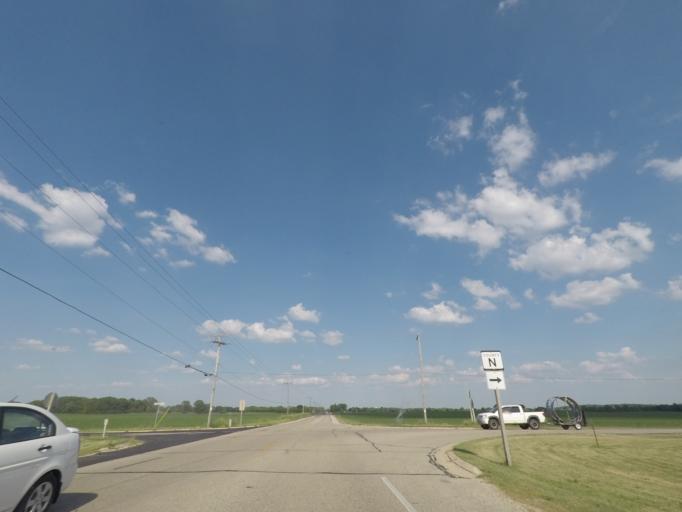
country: US
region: Wisconsin
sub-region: Walworth County
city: East Troy
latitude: 42.7927
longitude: -88.4453
